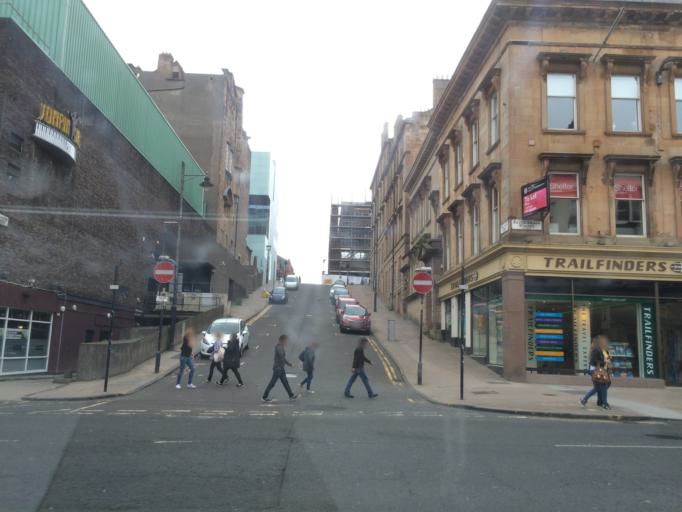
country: GB
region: Scotland
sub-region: Glasgow City
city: Glasgow
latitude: 55.8654
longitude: -4.2632
